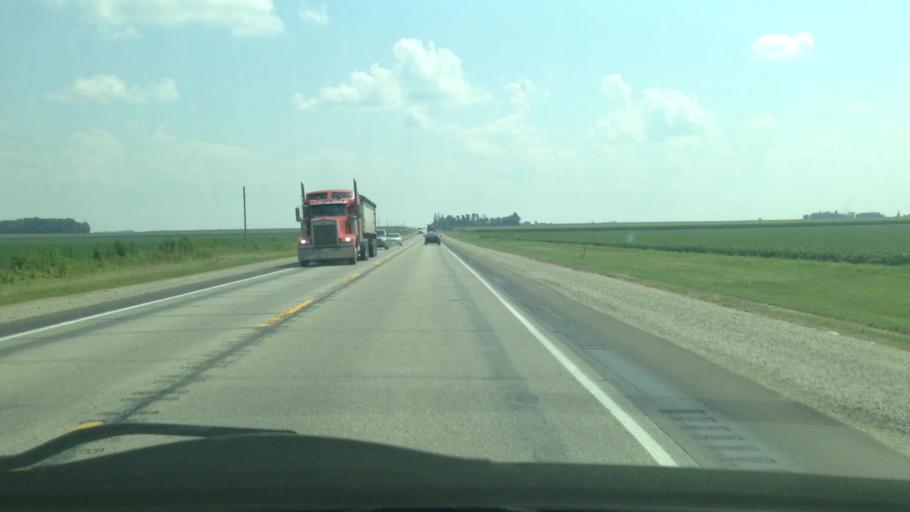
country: US
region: Iowa
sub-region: Howard County
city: Cresco
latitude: 43.4187
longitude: -92.2987
